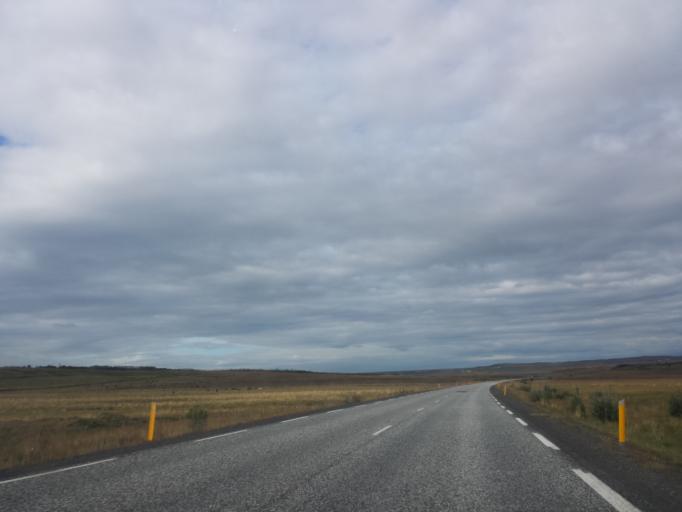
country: IS
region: West
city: Borgarnes
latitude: 64.3650
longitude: -21.8226
